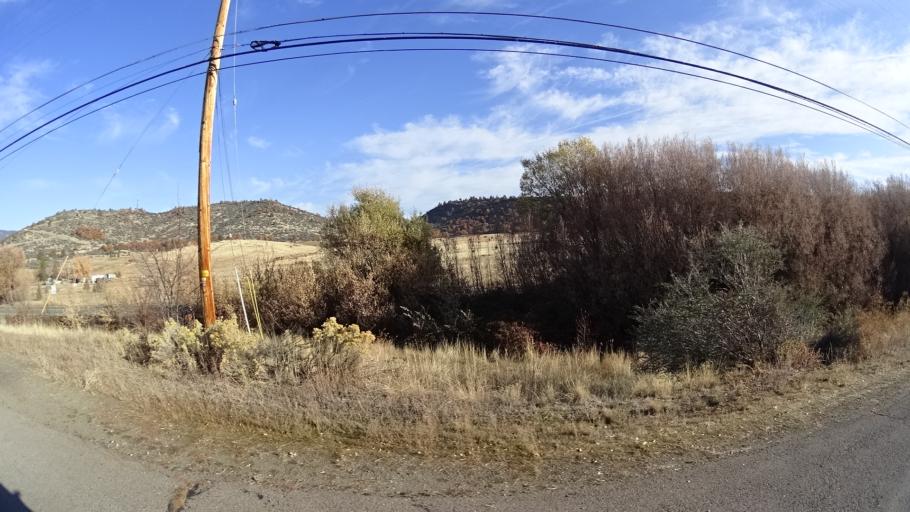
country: US
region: California
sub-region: Siskiyou County
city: Yreka
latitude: 41.7134
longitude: -122.6270
